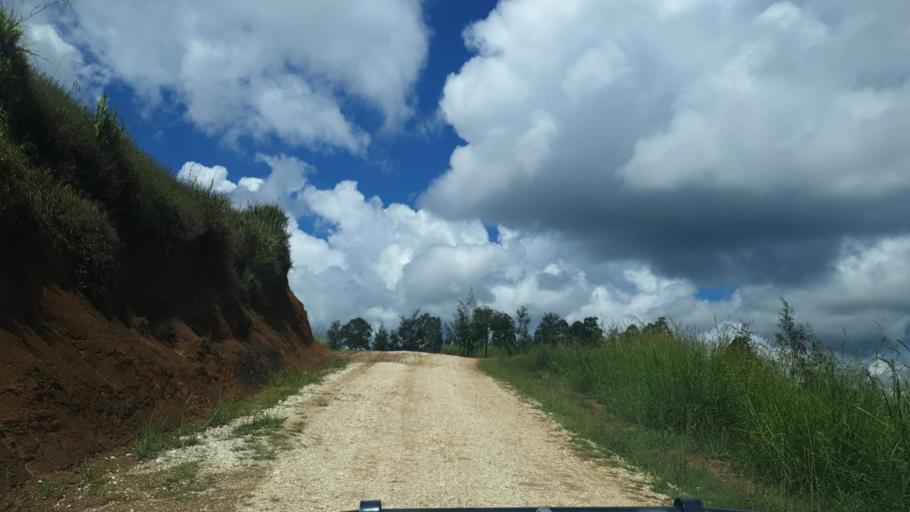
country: PG
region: Chimbu
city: Kundiawa
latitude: -6.2163
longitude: 145.1367
